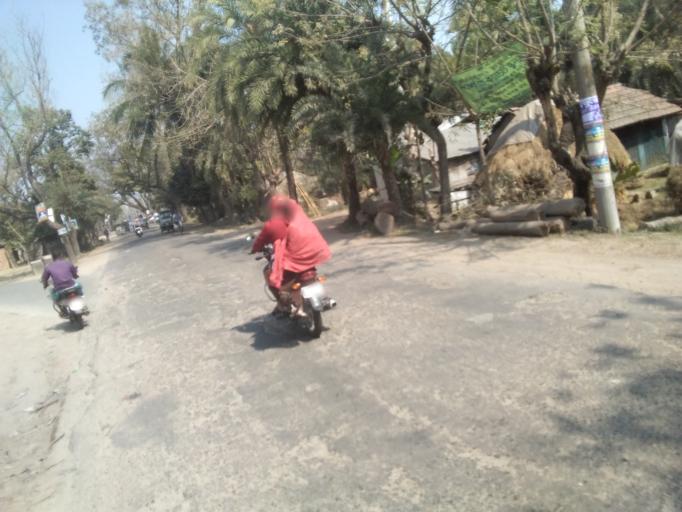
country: IN
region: West Bengal
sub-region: North 24 Parganas
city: Taki
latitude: 22.5901
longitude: 88.9998
